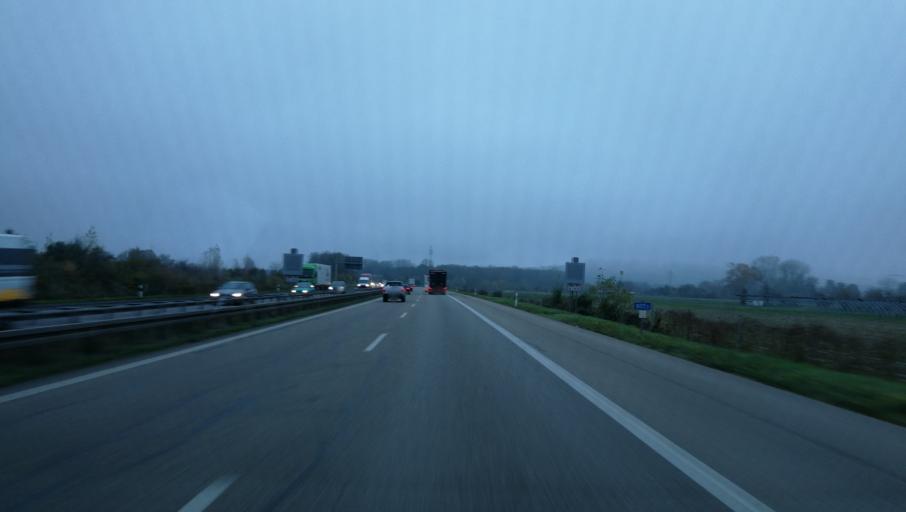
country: DE
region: Baden-Wuerttemberg
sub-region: Freiburg Region
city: Efringen-Kirchen
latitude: 47.6365
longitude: 7.5659
